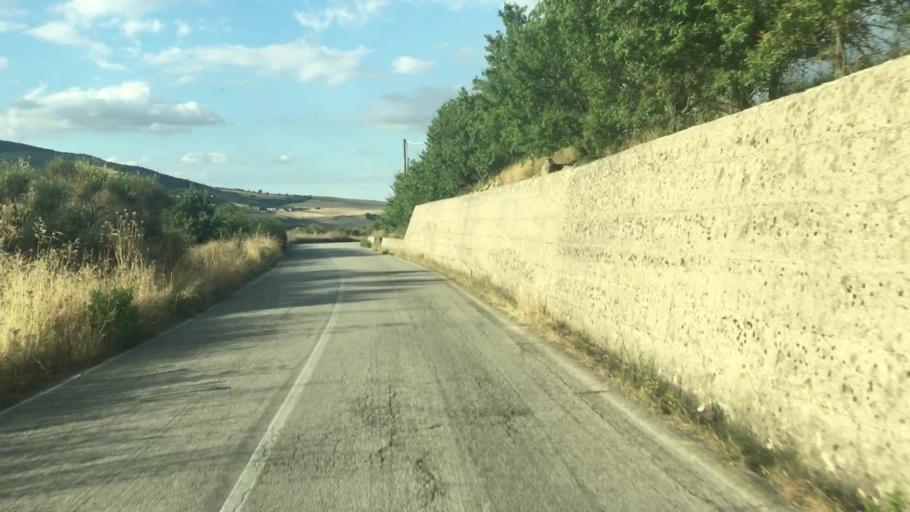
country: IT
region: Basilicate
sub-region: Provincia di Potenza
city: Tolve
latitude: 40.6963
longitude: 15.9930
